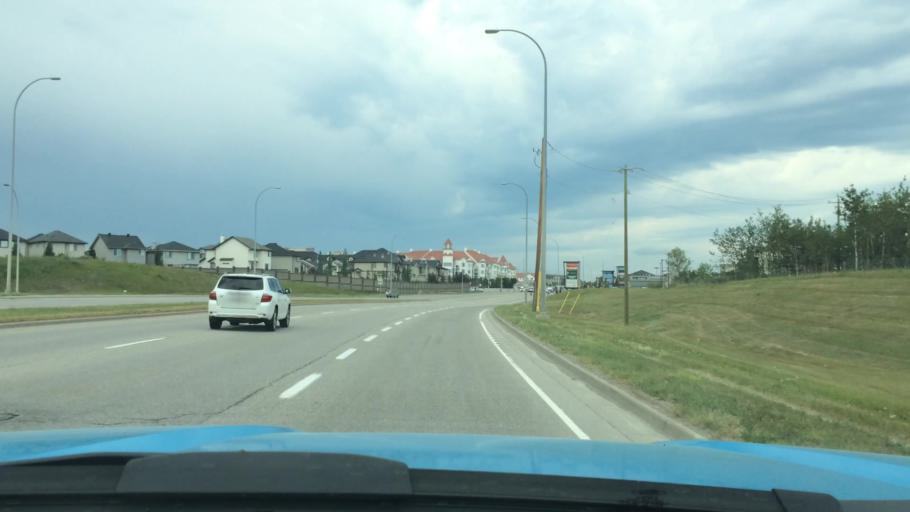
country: CA
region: Alberta
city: Calgary
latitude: 51.1474
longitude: -114.2102
